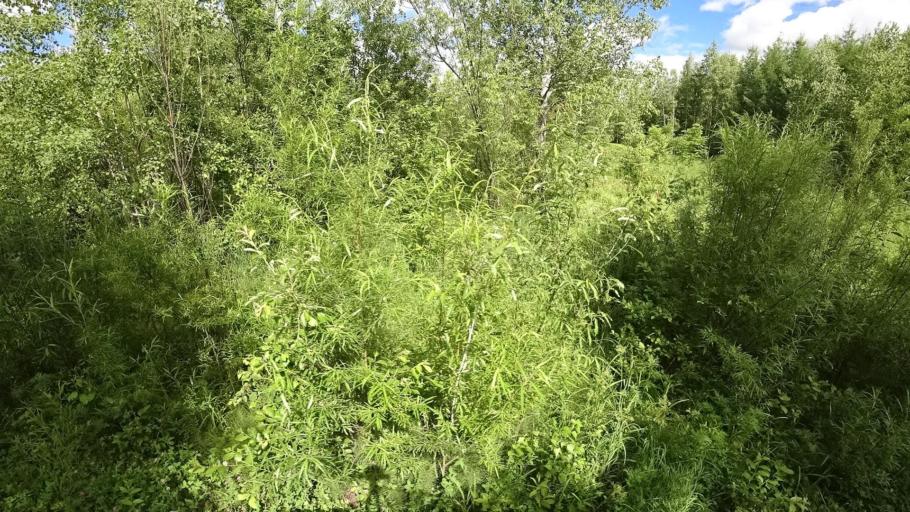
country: RU
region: Khabarovsk Krai
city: Litovko
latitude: 49.3670
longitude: 135.1688
